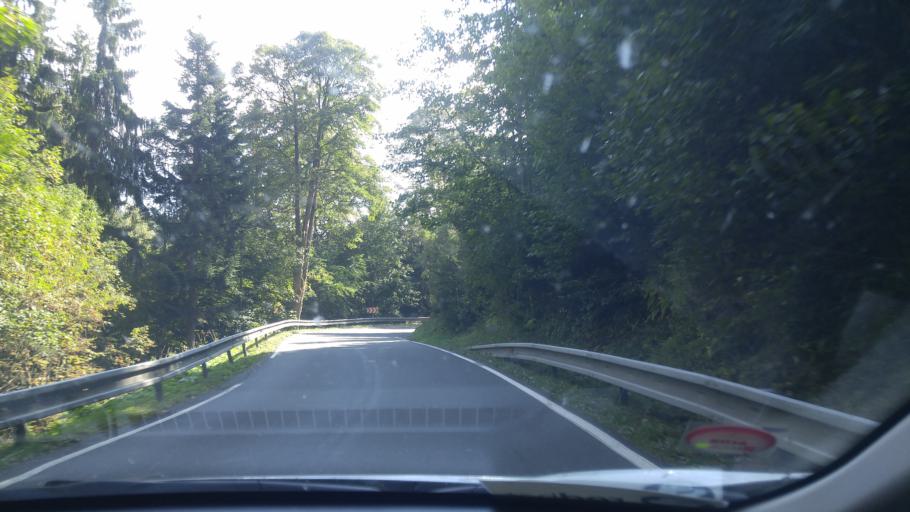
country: CZ
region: Olomoucky
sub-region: Okres Sumperk
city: Stare Mesto
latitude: 50.1657
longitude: 17.0271
